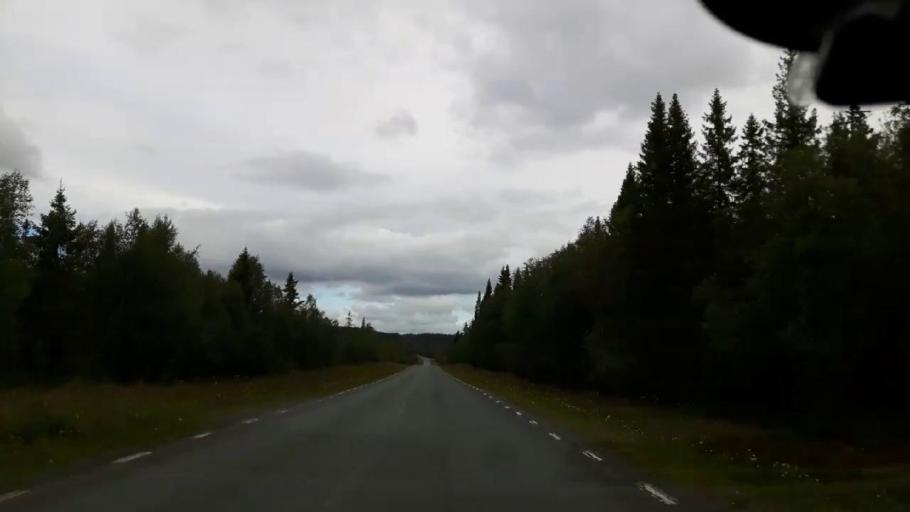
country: SE
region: Jaemtland
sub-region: Krokoms Kommun
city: Valla
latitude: 63.5617
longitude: 13.8471
